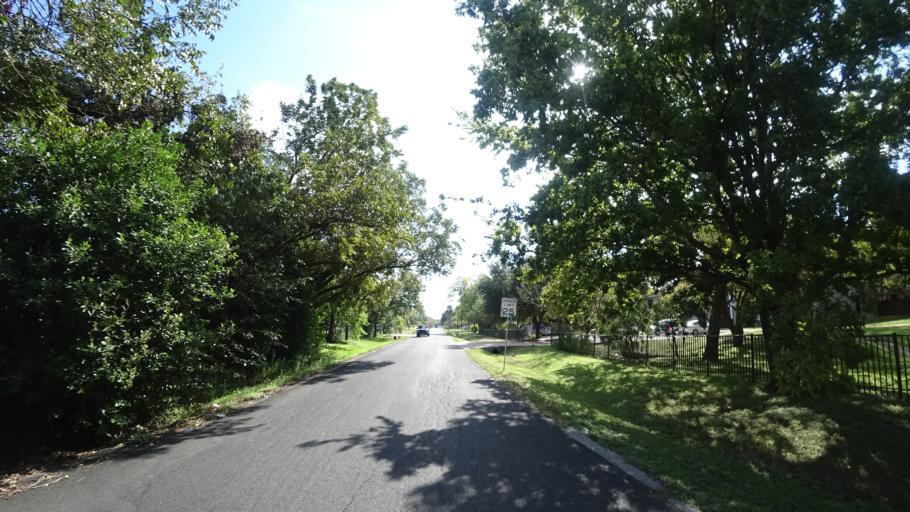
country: US
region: Texas
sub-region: Travis County
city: Rollingwood
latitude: 30.2088
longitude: -97.7840
